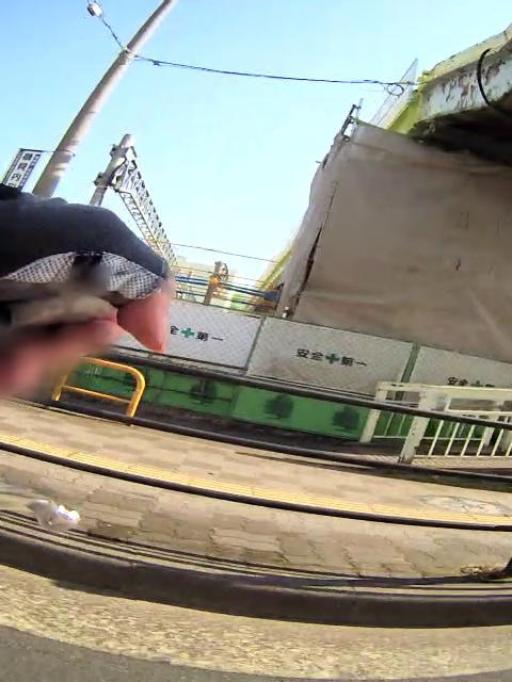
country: JP
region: Osaka
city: Suita
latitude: 34.7382
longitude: 135.5030
